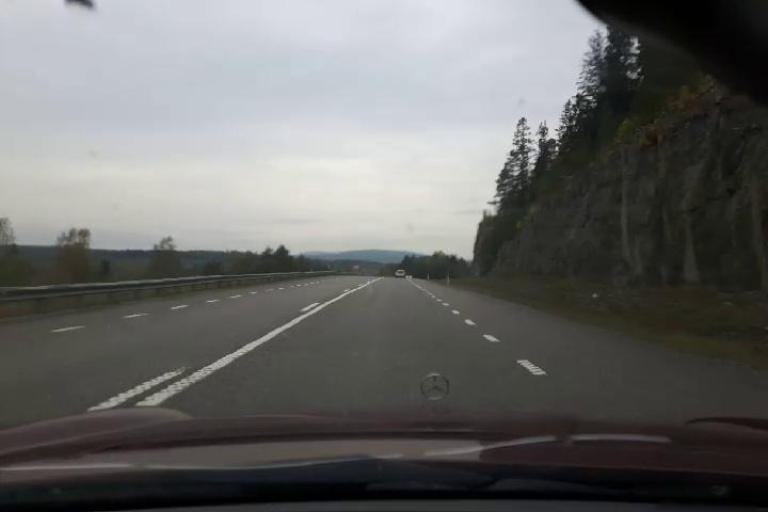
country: SE
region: Vaesternorrland
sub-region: Kramfors Kommun
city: Nordingra
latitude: 63.0074
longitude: 18.2276
